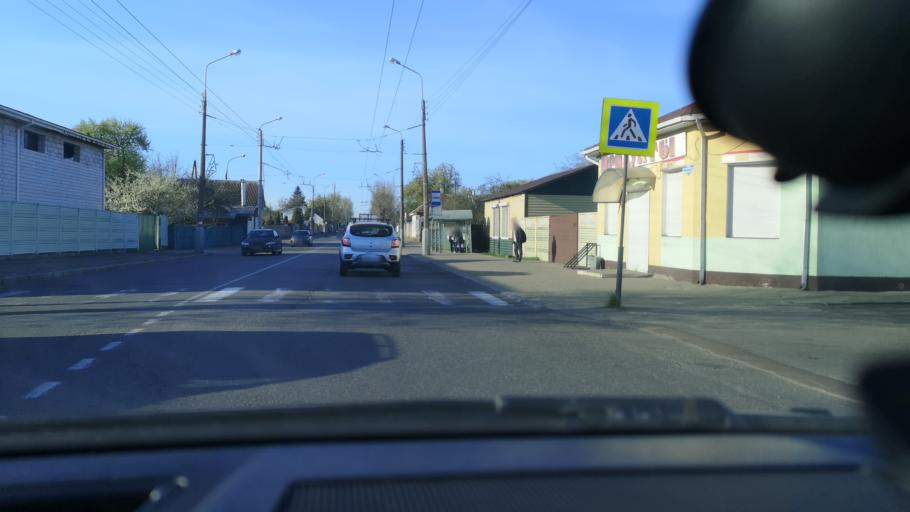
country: BY
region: Gomel
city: Gomel
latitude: 52.4376
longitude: 30.9773
